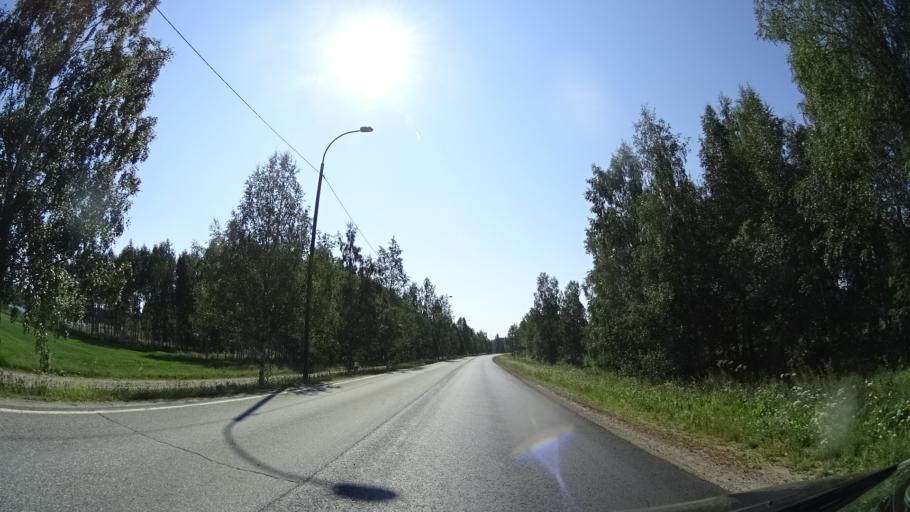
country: FI
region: North Karelia
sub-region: Joensuu
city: Juuka
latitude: 63.2435
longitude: 29.2751
